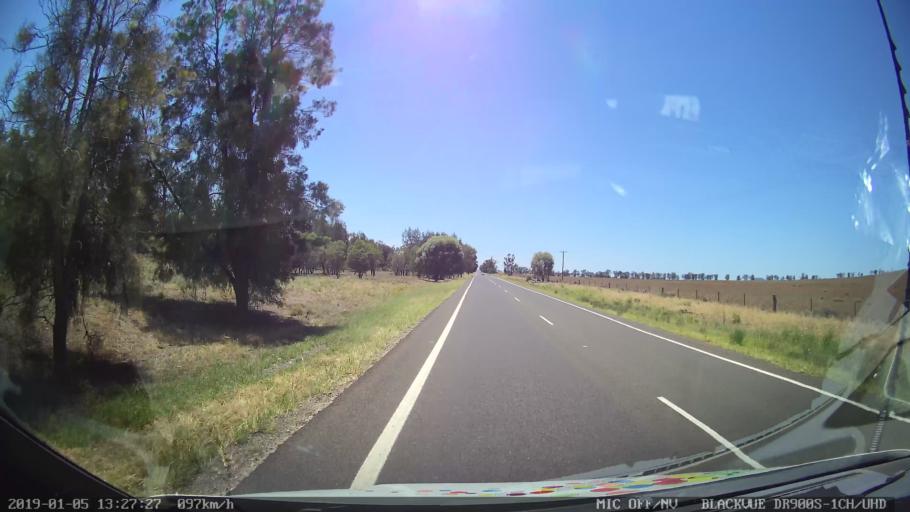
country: AU
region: New South Wales
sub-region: Gunnedah
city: Gunnedah
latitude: -31.0445
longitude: 150.0294
